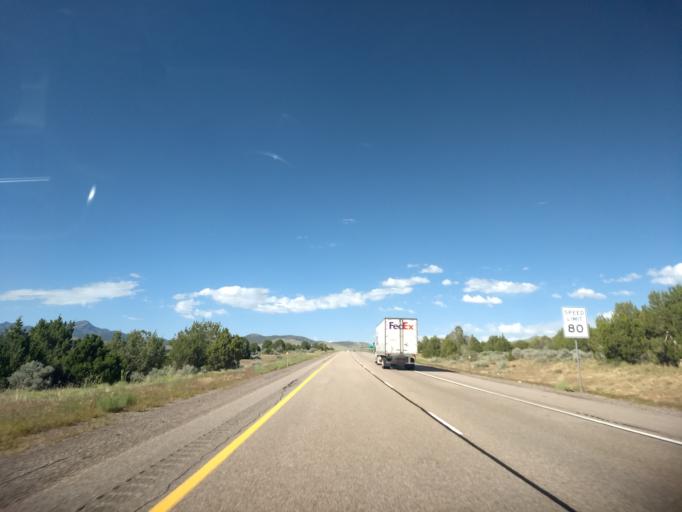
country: US
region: Utah
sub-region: Millard County
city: Fillmore
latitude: 39.1547
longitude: -112.2282
